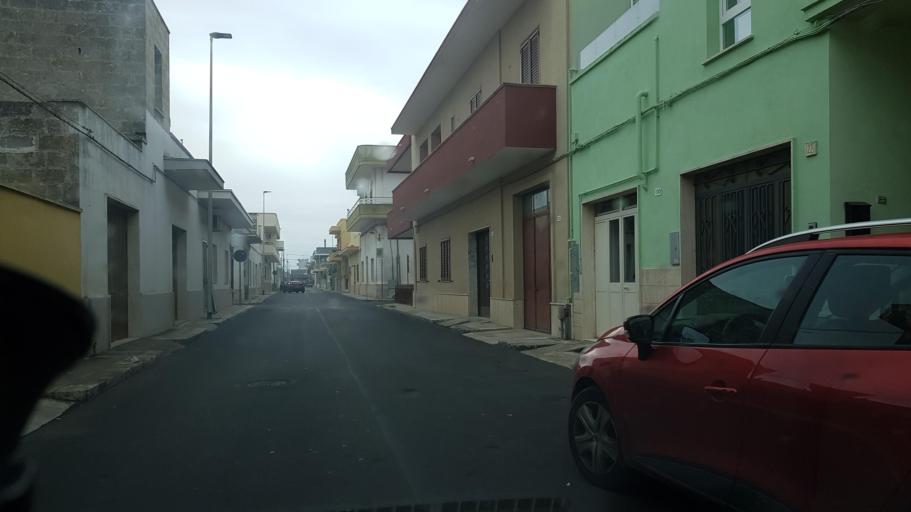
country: IT
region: Apulia
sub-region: Provincia di Lecce
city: Leverano
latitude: 40.2852
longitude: 17.9923
